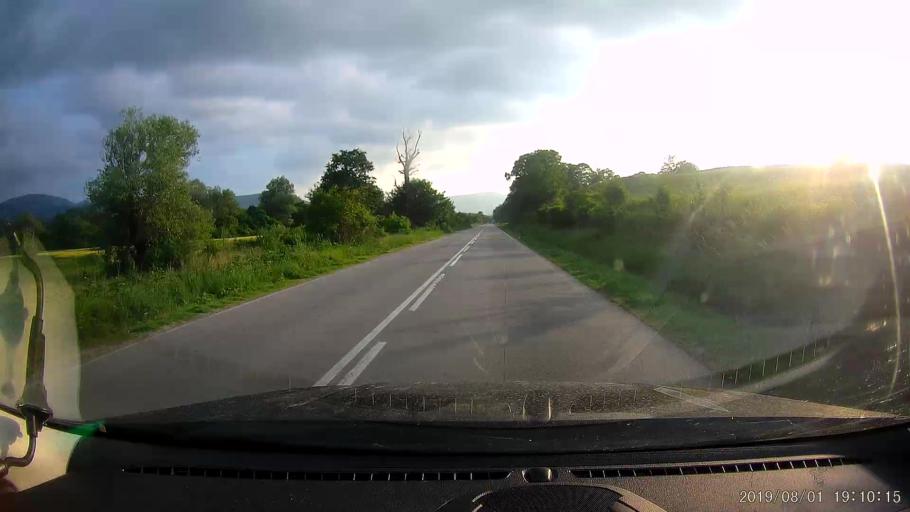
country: BG
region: Shumen
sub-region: Obshtina Smyadovo
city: Smyadovo
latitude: 42.9821
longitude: 26.9843
